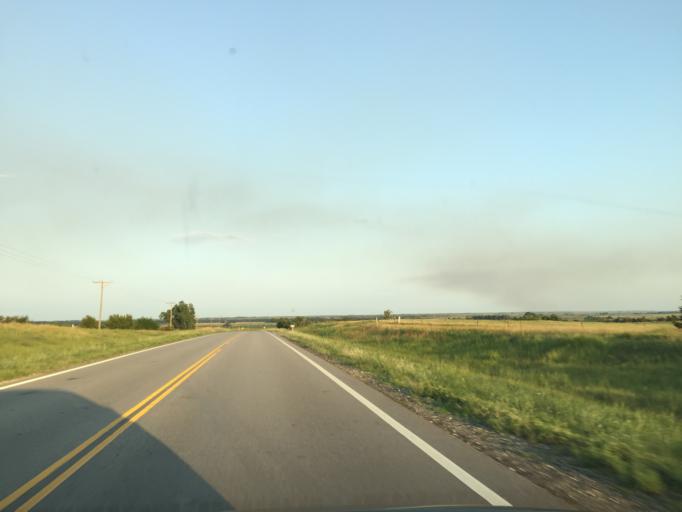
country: US
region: Kansas
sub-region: Ellsworth County
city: Ellsworth
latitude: 38.6973
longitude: -98.2112
